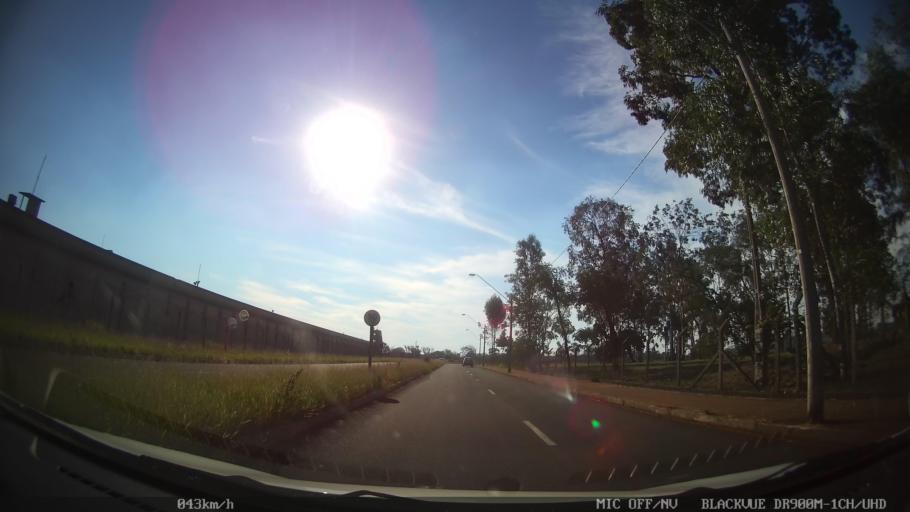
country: BR
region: Sao Paulo
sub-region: Araraquara
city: Araraquara
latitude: -21.7630
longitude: -48.1354
